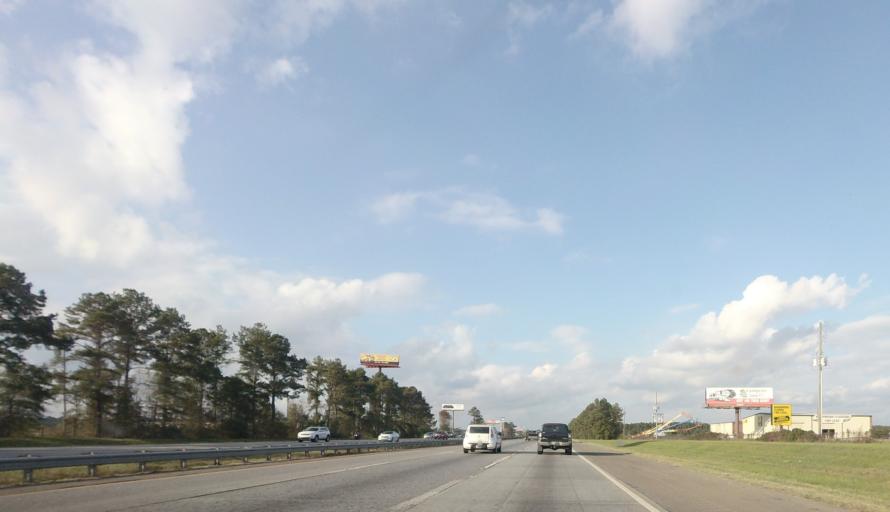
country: US
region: Georgia
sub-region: Peach County
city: Byron
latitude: 32.6457
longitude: -83.7437
